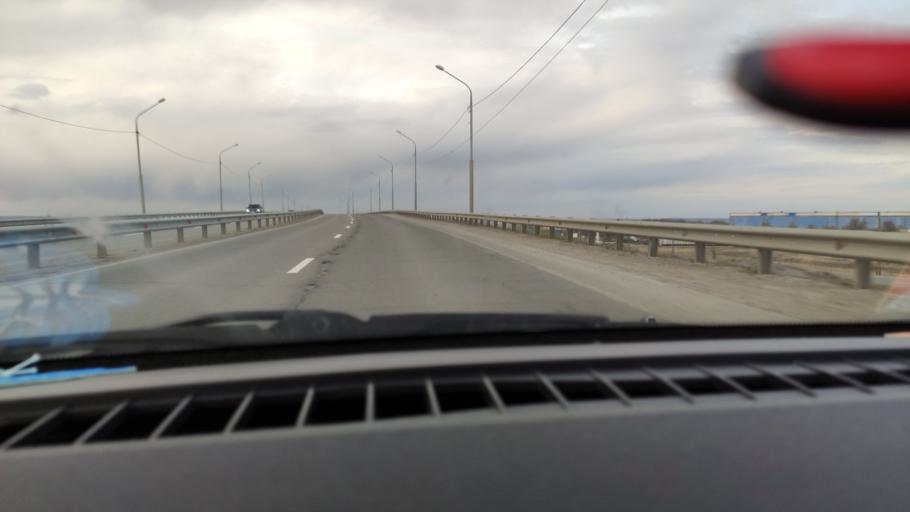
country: RU
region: Saratov
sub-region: Saratovskiy Rayon
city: Saratov
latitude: 51.6436
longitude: 45.9855
